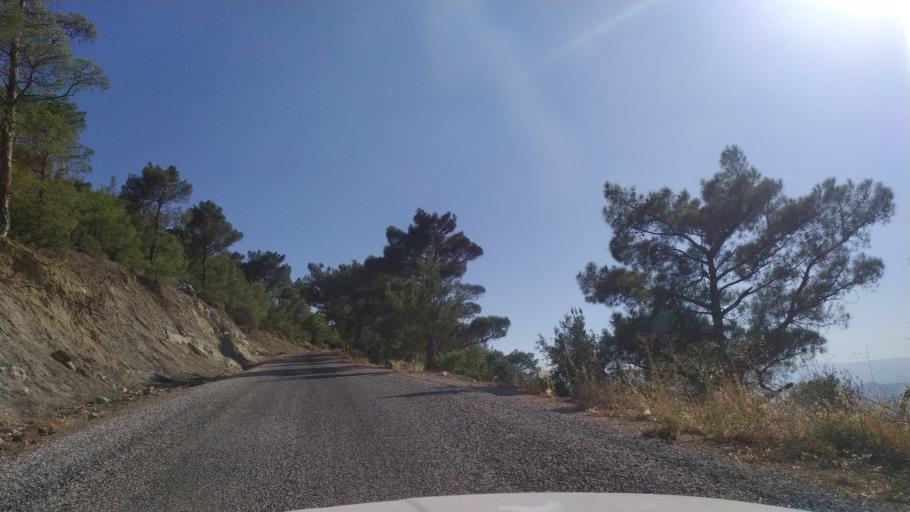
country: TR
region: Mersin
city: Mut
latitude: 36.7032
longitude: 33.4721
